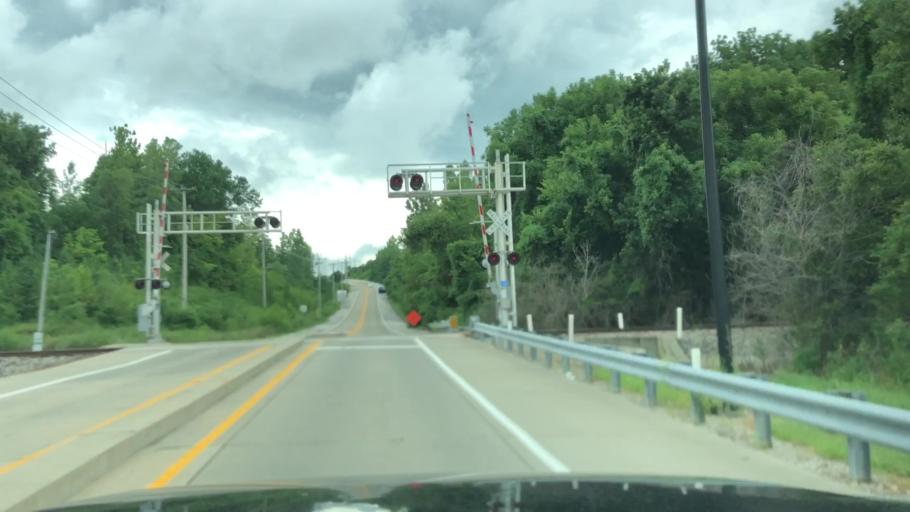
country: US
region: Missouri
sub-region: Saint Charles County
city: Saint Peters
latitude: 38.8044
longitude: -90.5809
